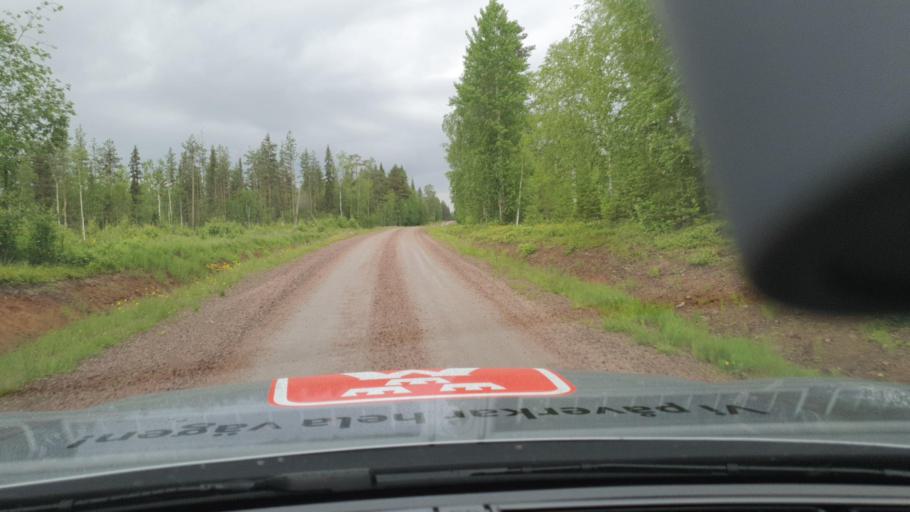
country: SE
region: Norrbotten
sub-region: Overkalix Kommun
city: OEverkalix
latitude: 66.6147
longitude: 22.7329
